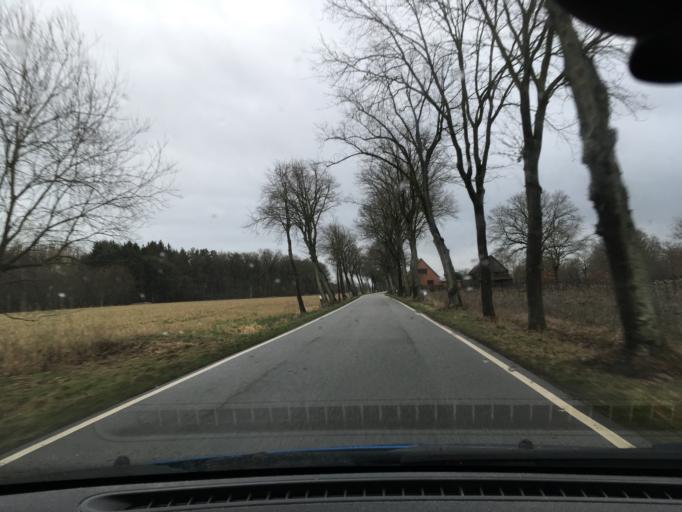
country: DE
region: Schleswig-Holstein
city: Lanze
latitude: 53.3623
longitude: 10.6128
